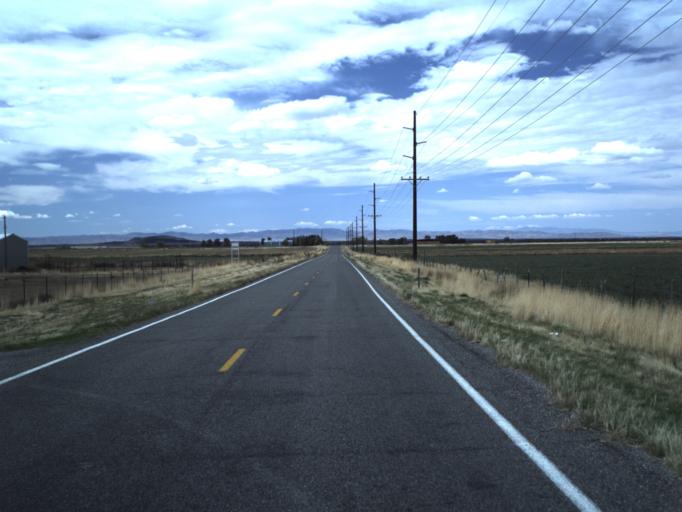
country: US
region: Utah
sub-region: Millard County
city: Fillmore
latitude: 38.9792
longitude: -112.4005
